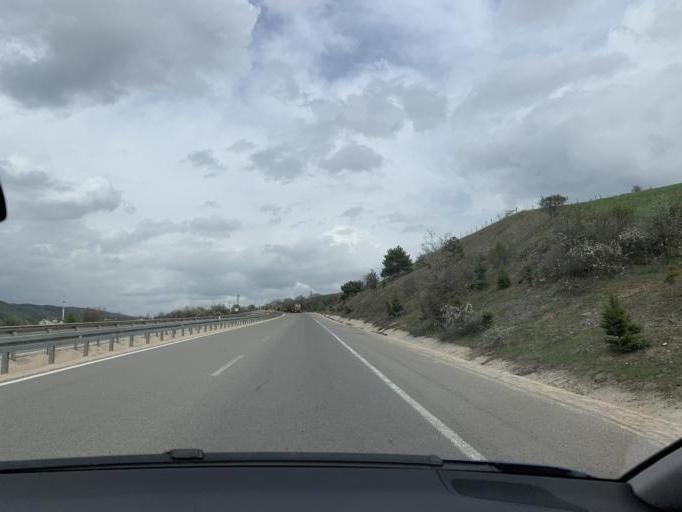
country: TR
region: Bolu
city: Gerede
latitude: 40.7869
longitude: 32.1194
